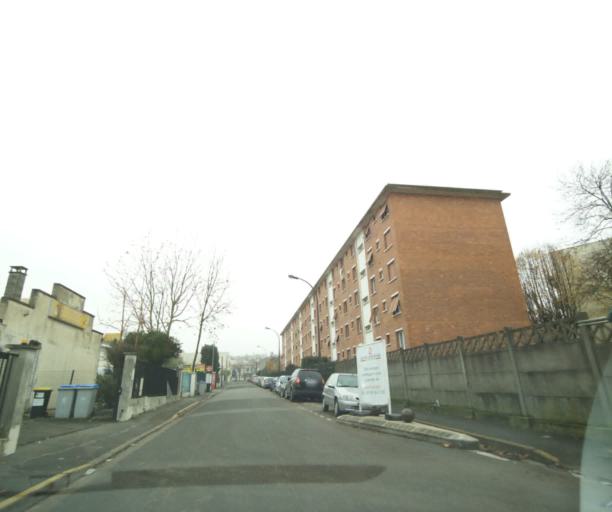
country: FR
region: Ile-de-France
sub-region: Departement de Seine-Saint-Denis
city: Livry-Gargan
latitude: 48.9259
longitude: 2.5461
